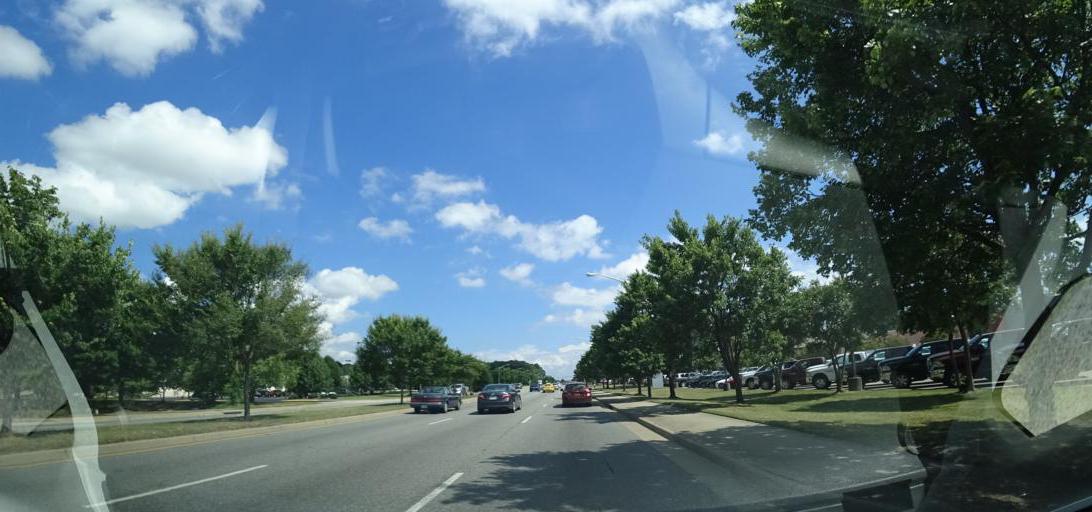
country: US
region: Virginia
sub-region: York County
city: Yorktown
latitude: 37.1341
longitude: -76.5167
